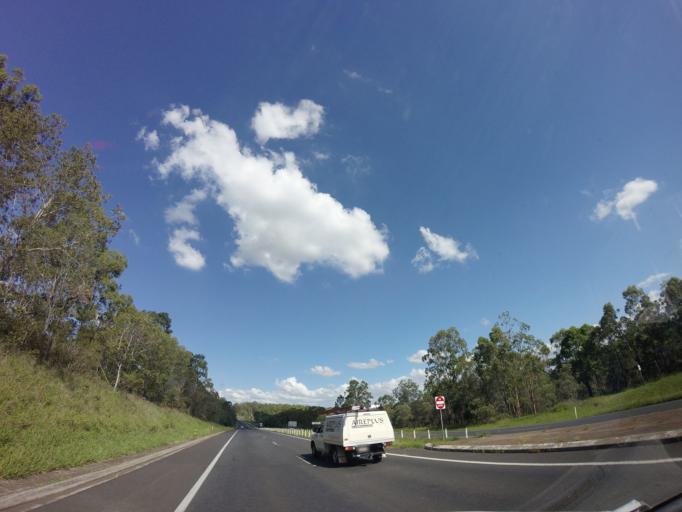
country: AU
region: Queensland
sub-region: Ipswich
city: Thagoona
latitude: -27.5767
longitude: 152.6774
